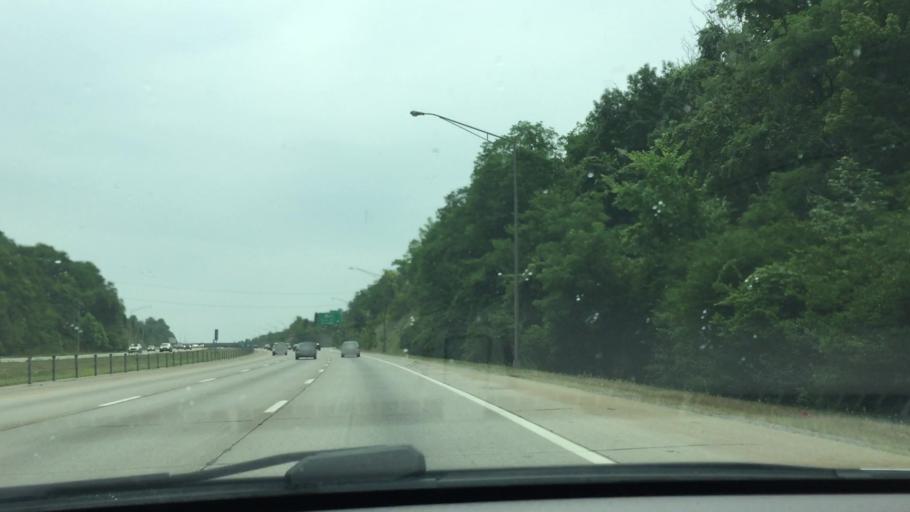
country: US
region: Kentucky
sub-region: Kenton County
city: Fort Wright
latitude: 39.0238
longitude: -84.5218
